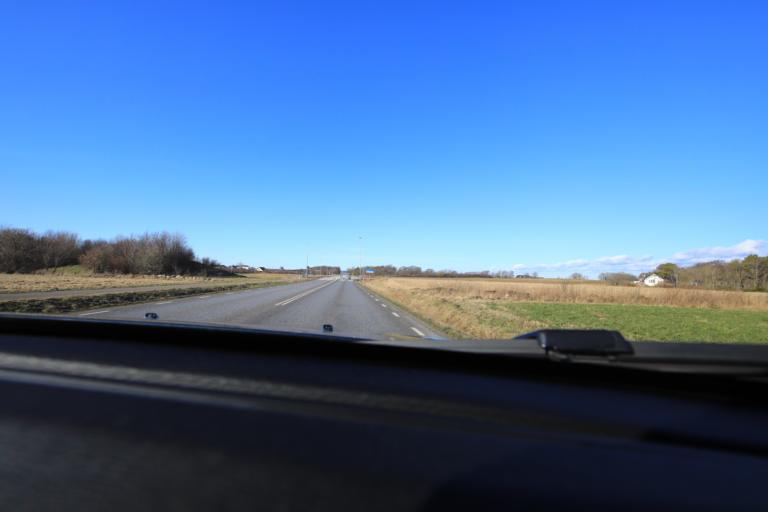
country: SE
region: Halland
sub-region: Varbergs Kommun
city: Traslovslage
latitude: 57.0623
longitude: 12.2952
